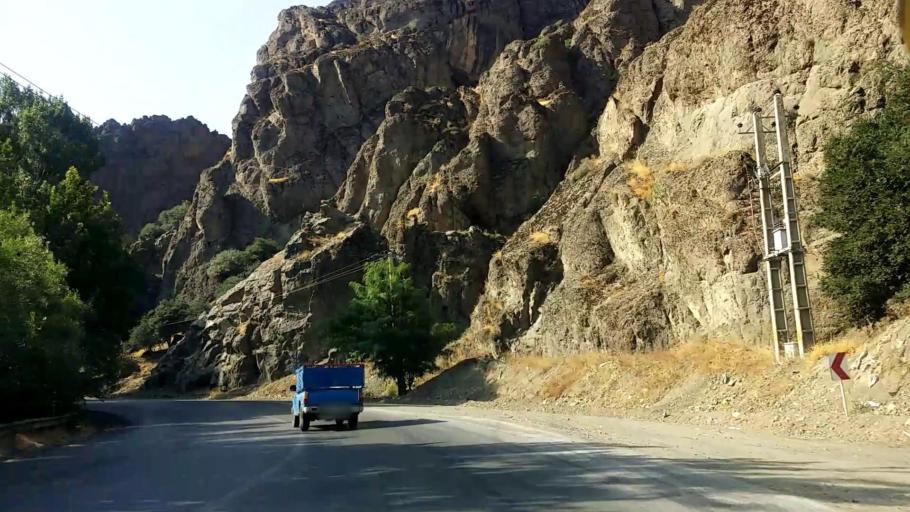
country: IR
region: Alborz
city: Karaj
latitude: 35.8794
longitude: 51.0415
